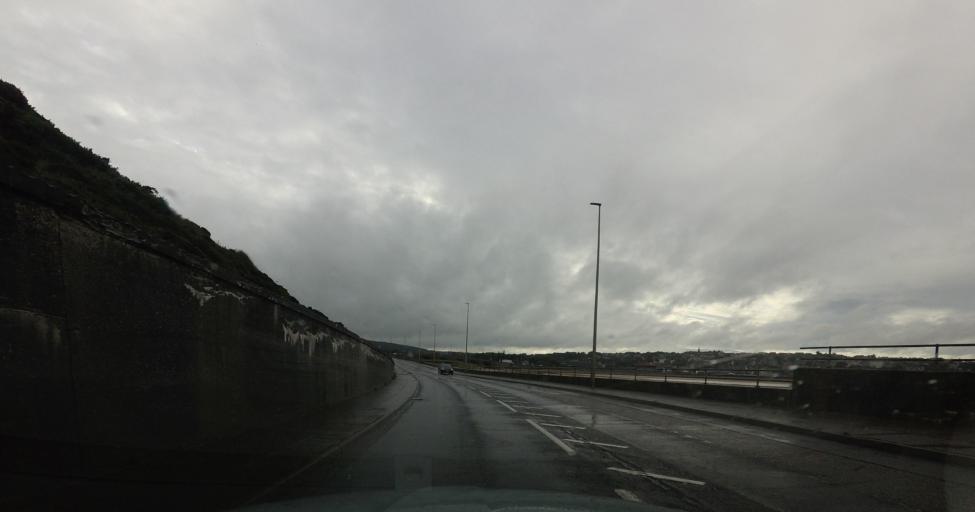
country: GB
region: Scotland
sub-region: Aberdeenshire
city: Macduff
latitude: 57.6654
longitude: -2.5096
